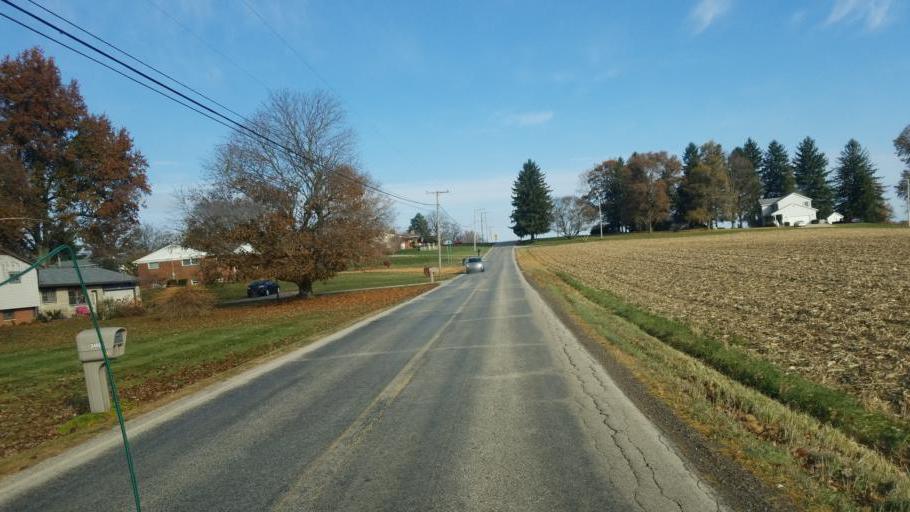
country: US
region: Ohio
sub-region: Richland County
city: Lexington
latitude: 40.6924
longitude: -82.5352
